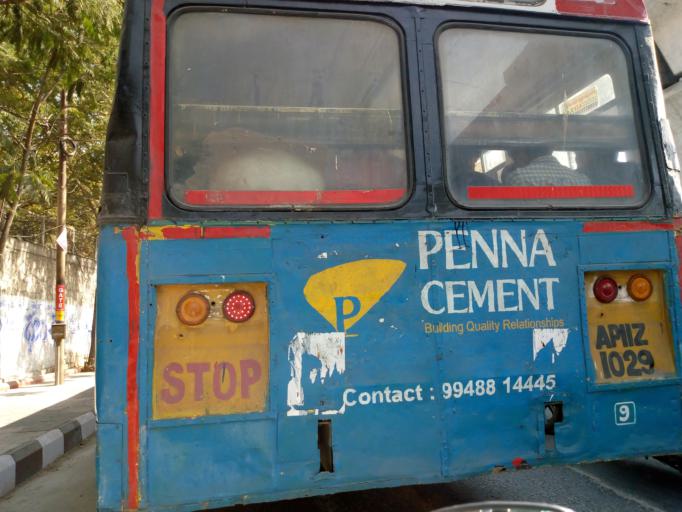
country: IN
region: Telangana
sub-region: Rangareddi
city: Uppal Kalan
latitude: 17.4217
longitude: 78.5396
